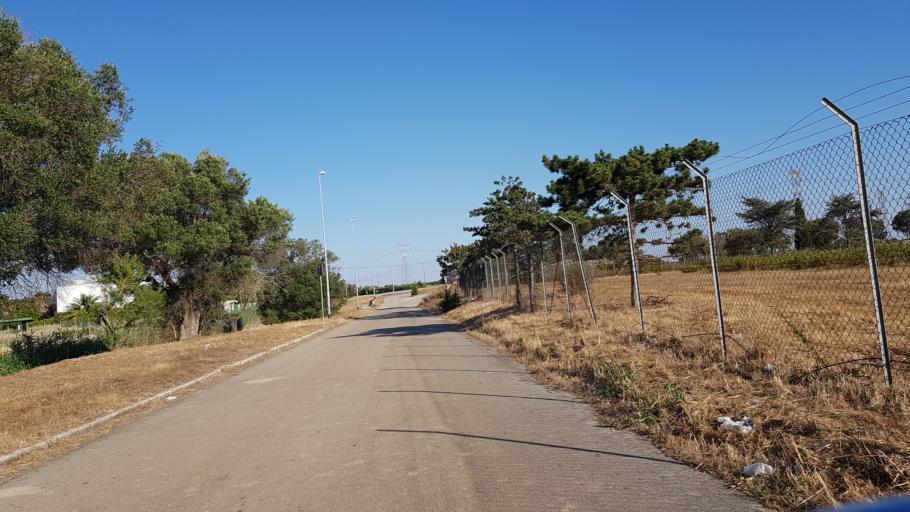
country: IT
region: Apulia
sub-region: Provincia di Brindisi
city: Tuturano
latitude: 40.5606
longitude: 18.0196
